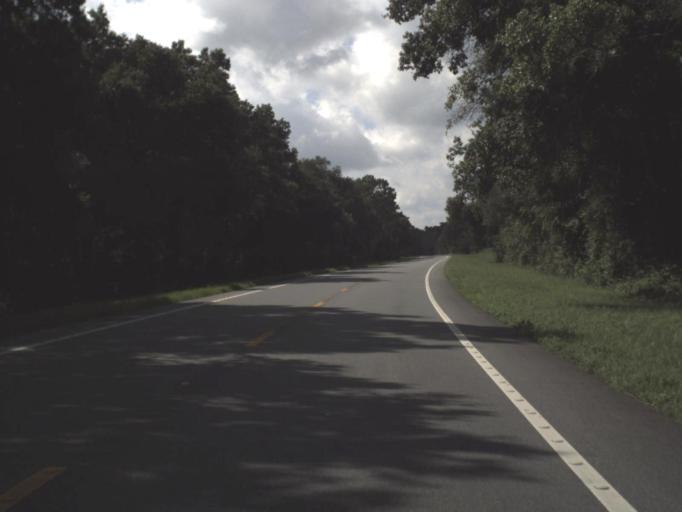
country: US
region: Florida
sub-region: Citrus County
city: Hernando
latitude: 28.9284
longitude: -82.3923
